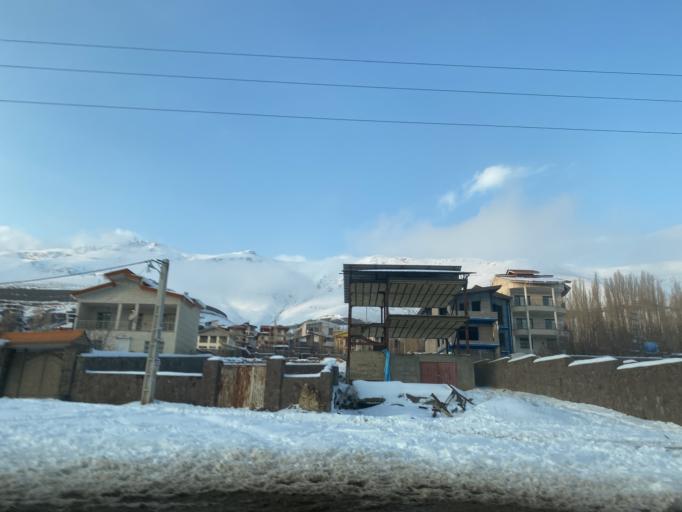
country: IR
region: Tehran
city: Damavand
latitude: 35.7705
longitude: 52.0100
